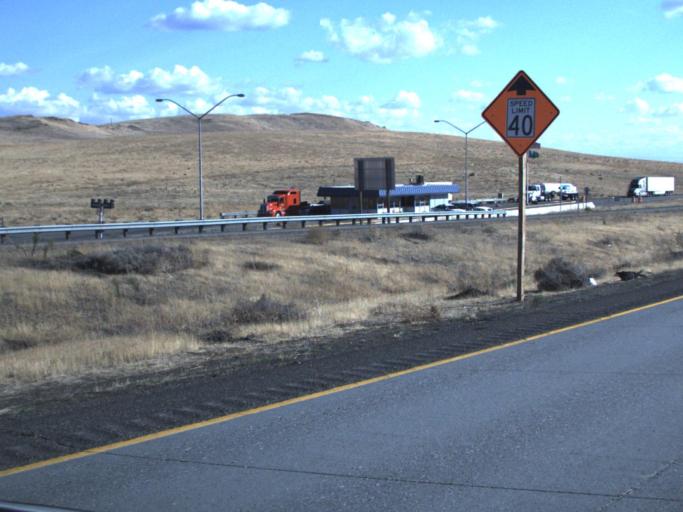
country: US
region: Oregon
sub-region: Umatilla County
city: Umatilla
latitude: 45.9598
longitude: -119.3422
